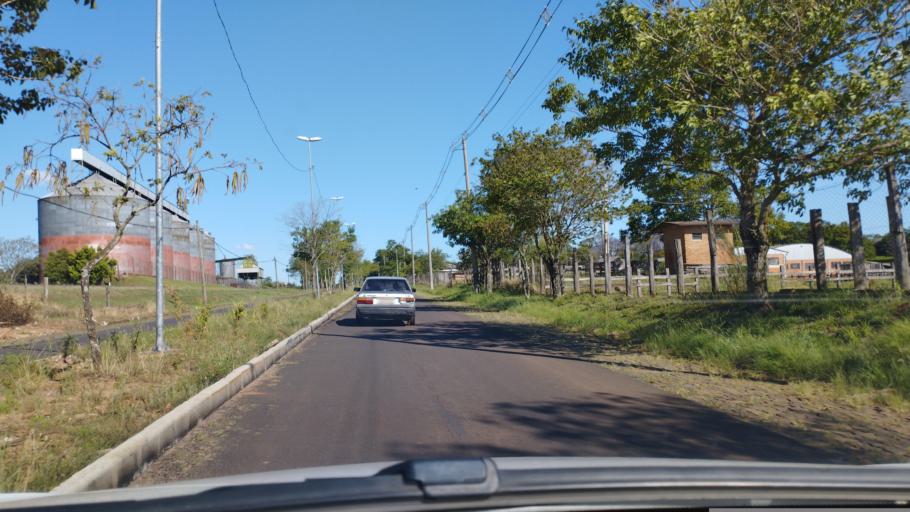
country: BR
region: Rio Grande do Sul
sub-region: Tupancireta
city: Tupancireta
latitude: -29.0718
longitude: -53.8423
